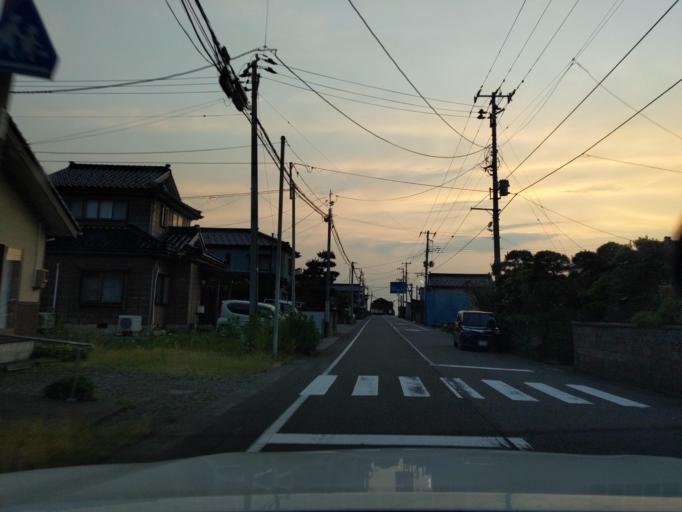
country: JP
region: Niigata
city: Kashiwazaki
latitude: 37.4567
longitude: 138.6128
